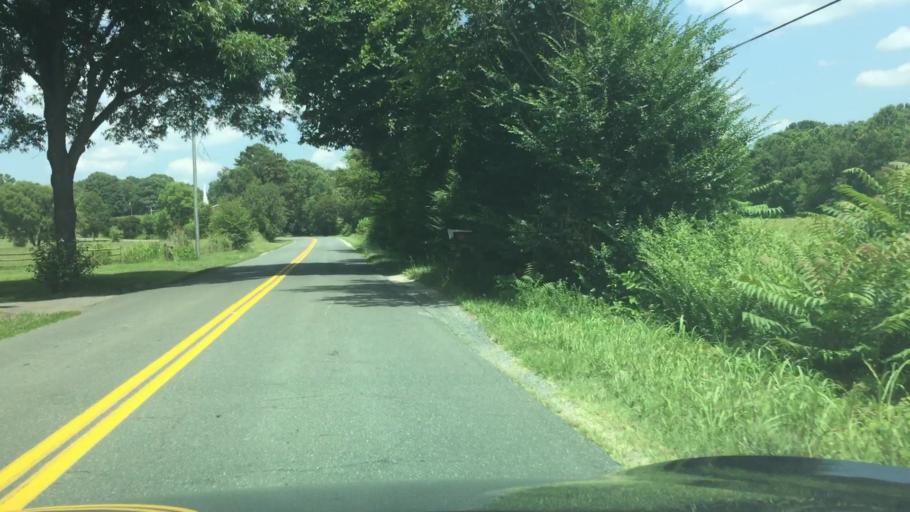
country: US
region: Virginia
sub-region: Campbell County
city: Concord
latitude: 37.3472
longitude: -78.9145
